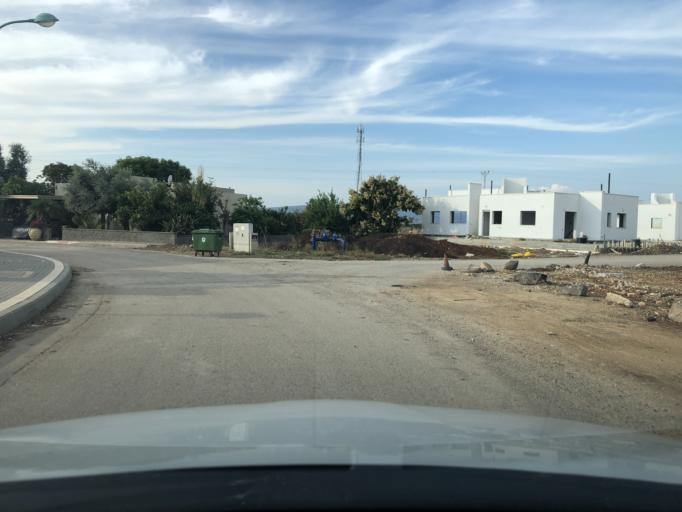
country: IL
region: Northern District
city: Yavne'el
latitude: 32.6628
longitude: 35.5862
